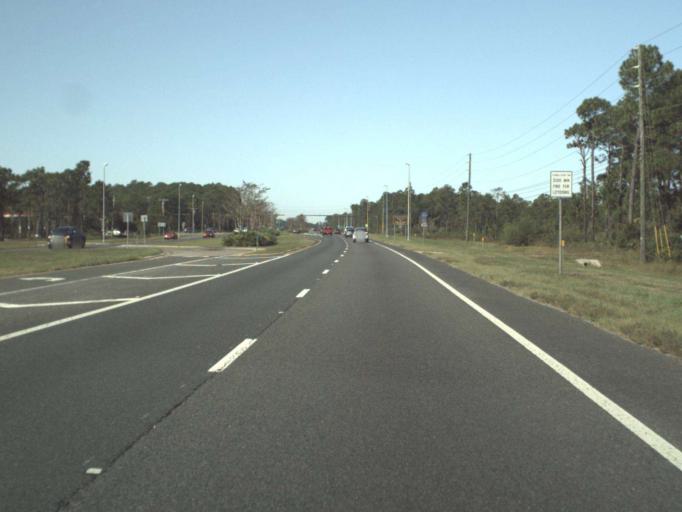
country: US
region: Florida
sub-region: Walton County
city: Miramar Beach
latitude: 30.3753
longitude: -86.2722
